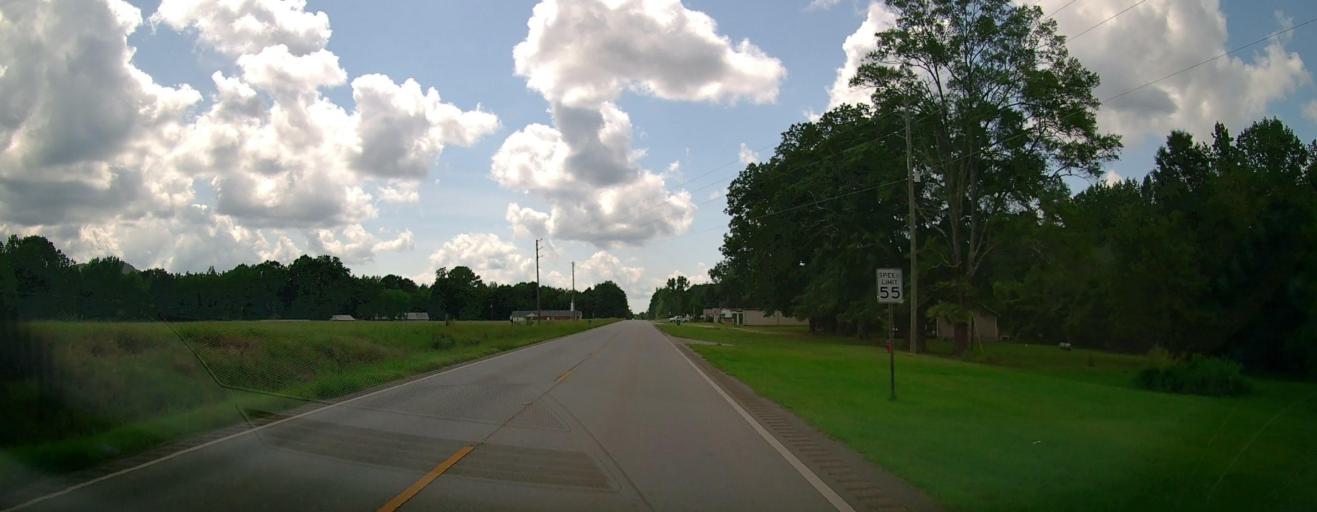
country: US
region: Georgia
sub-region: Carroll County
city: Bowdon
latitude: 33.5639
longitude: -85.4301
